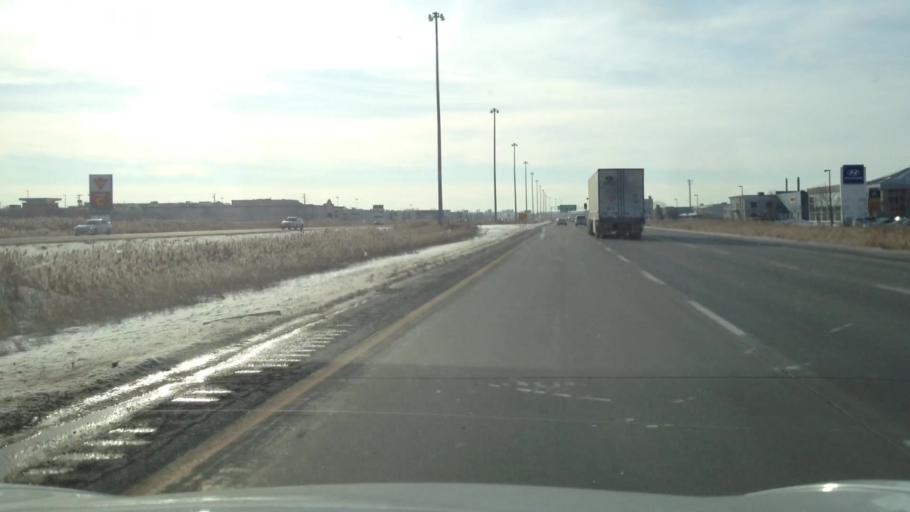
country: CA
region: Quebec
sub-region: Monteregie
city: Vaudreuil-Dorion
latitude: 45.4096
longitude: -74.0389
